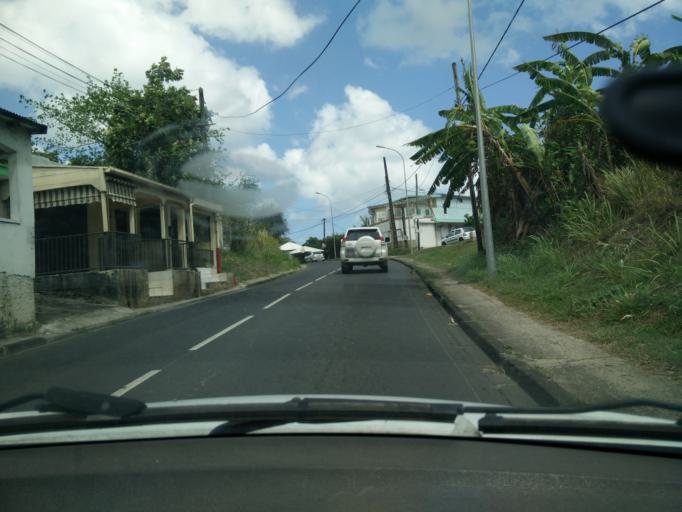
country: GP
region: Guadeloupe
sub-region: Guadeloupe
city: Les Abymes
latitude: 16.2622
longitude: -61.5020
